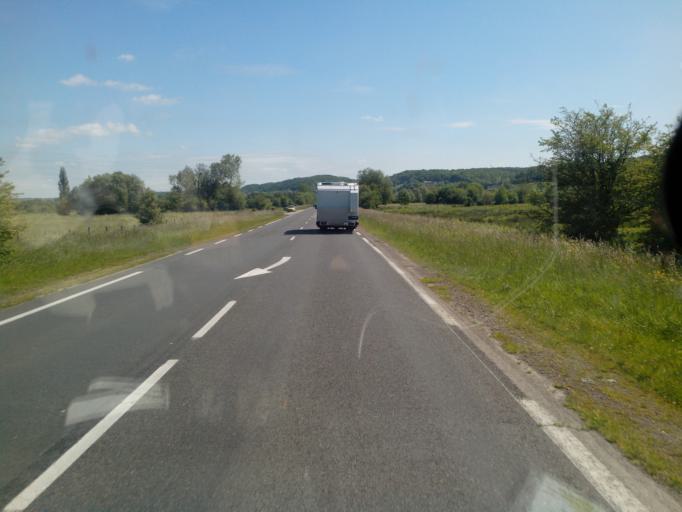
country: FR
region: Haute-Normandie
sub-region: Departement de l'Eure
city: Toutainville
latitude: 49.4135
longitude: 0.4238
